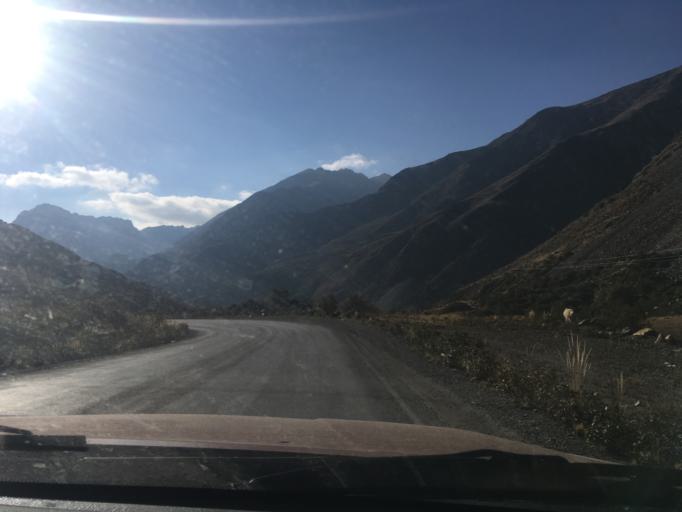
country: BO
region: La Paz
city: Quime
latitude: -17.0020
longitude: -67.2766
